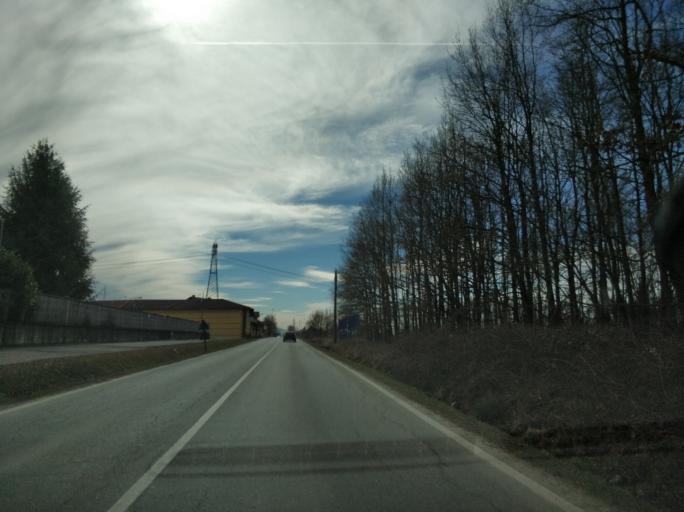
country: IT
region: Piedmont
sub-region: Provincia di Torino
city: Lombardore
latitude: 45.2167
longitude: 7.7305
